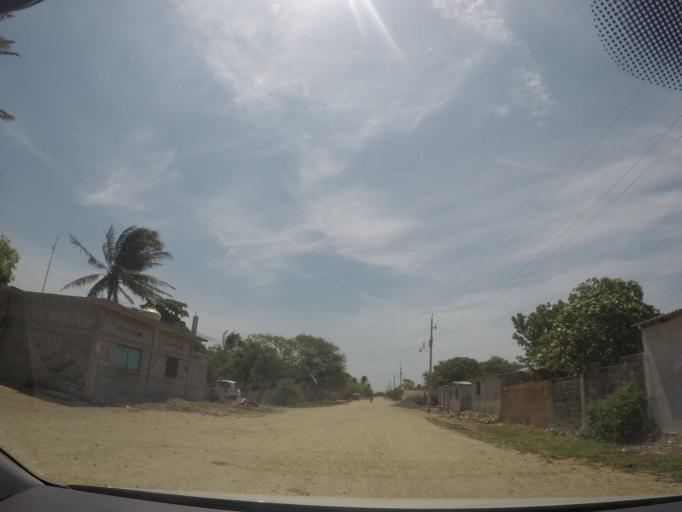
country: MX
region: Oaxaca
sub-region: Salina Cruz
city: Salina Cruz
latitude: 16.1903
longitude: -95.1198
